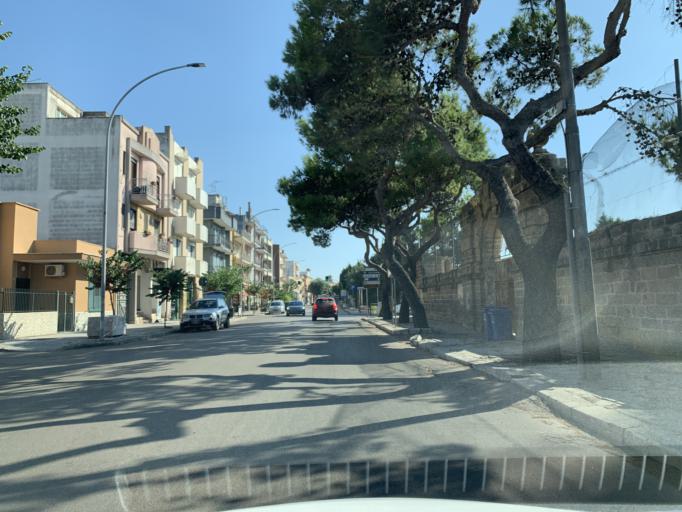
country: IT
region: Apulia
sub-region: Provincia di Lecce
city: Nardo
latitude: 40.1830
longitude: 18.0368
